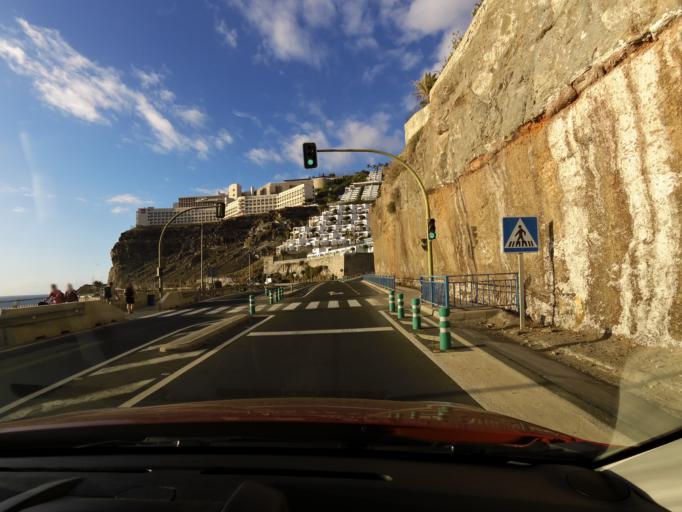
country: ES
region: Canary Islands
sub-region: Provincia de Las Palmas
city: Puerto Rico
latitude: 27.7857
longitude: -15.7192
